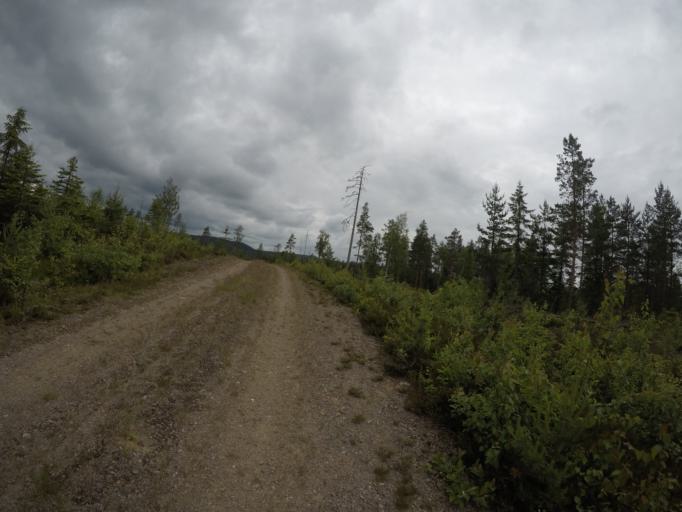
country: SE
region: Dalarna
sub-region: Ludvika Kommun
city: Abborrberget
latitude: 60.0877
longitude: 14.5087
